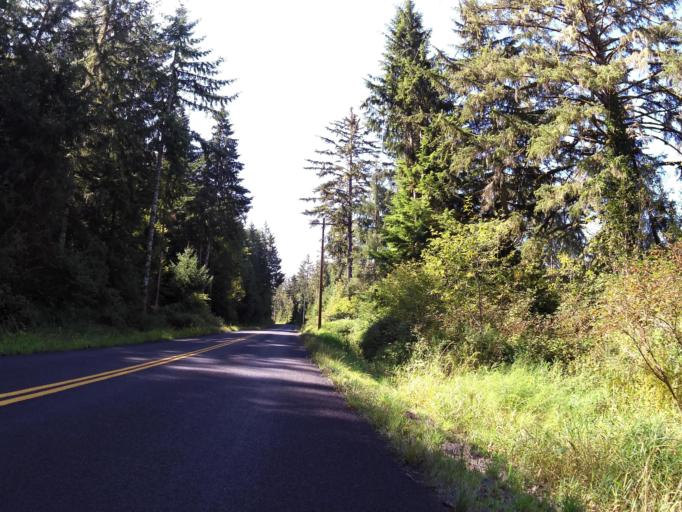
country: US
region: Washington
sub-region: Wahkiakum County
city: Cathlamet
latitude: 46.1920
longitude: -123.5756
